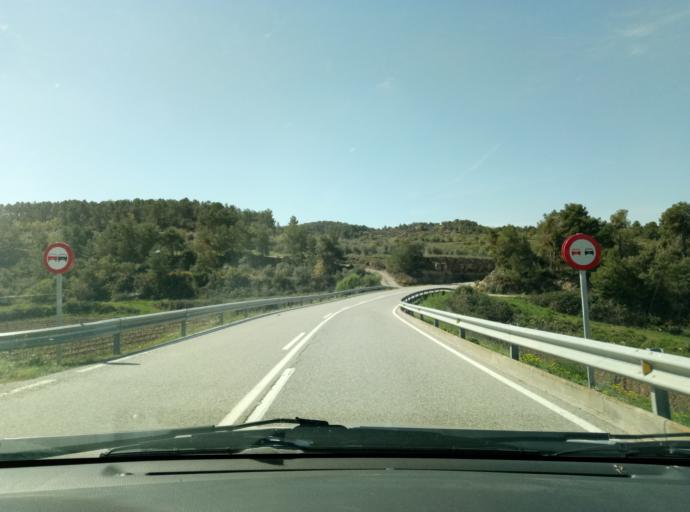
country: ES
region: Catalonia
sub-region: Provincia de Lleida
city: Fulleda
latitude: 41.5165
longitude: 1.0277
